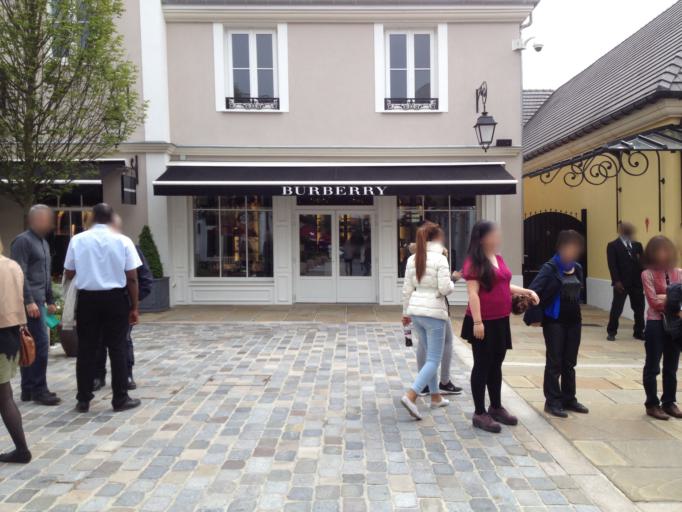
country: FR
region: Ile-de-France
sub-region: Departement de Seine-et-Marne
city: Serris
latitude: 48.8525
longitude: 2.7848
